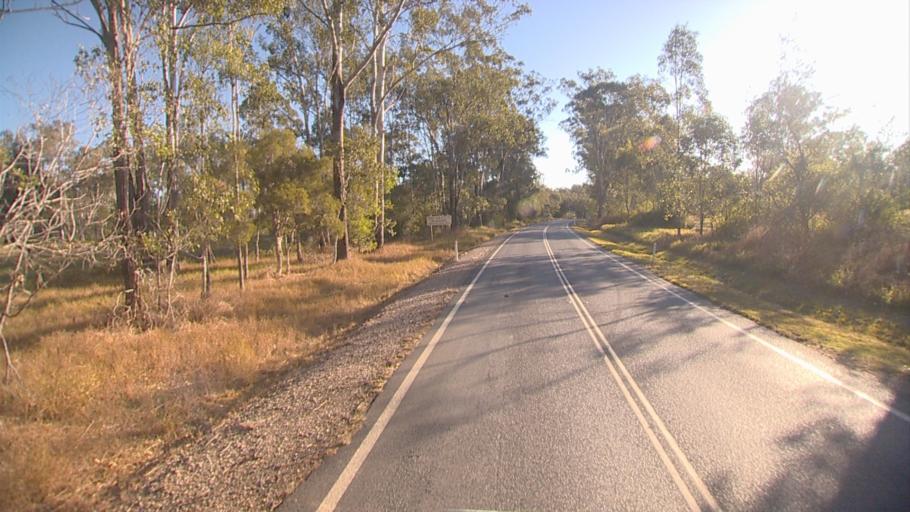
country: AU
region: Queensland
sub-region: Logan
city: Chambers Flat
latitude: -27.7807
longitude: 153.0647
